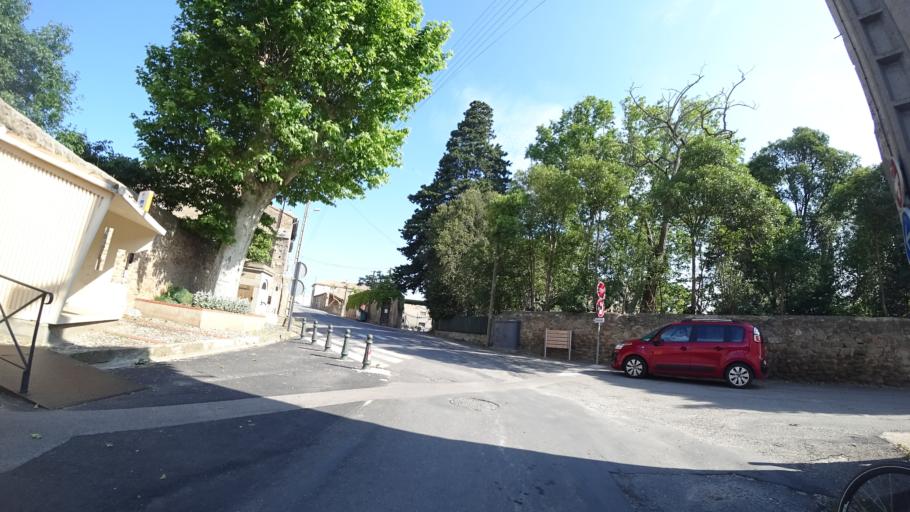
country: FR
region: Languedoc-Roussillon
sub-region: Departement de l'Herault
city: Olonzac
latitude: 43.2678
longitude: 2.7210
